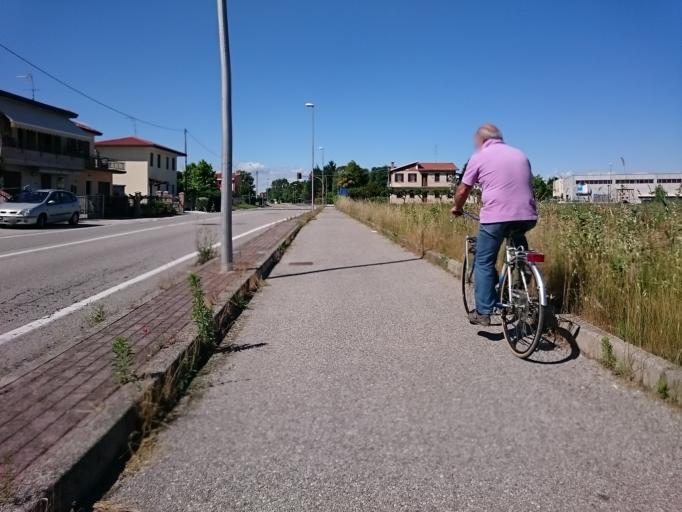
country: IT
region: Veneto
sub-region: Provincia di Venezia
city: Campolongo Maggiore Liettoli
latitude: 45.3338
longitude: 12.0206
